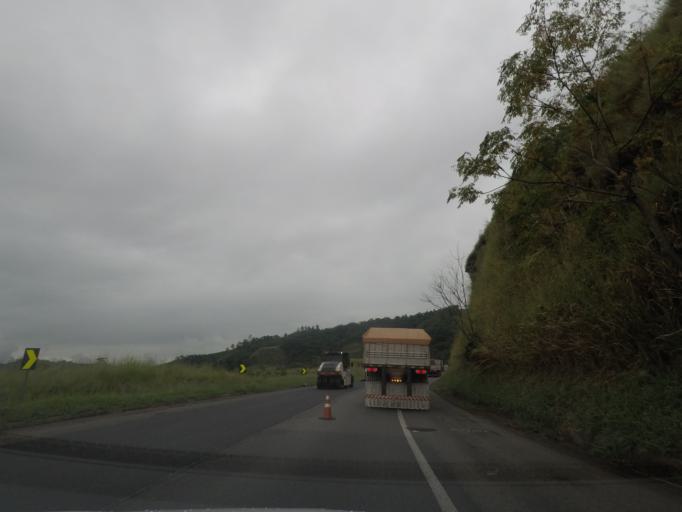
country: BR
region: Sao Paulo
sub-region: Cajati
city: Cajati
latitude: -24.8183
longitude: -48.2114
